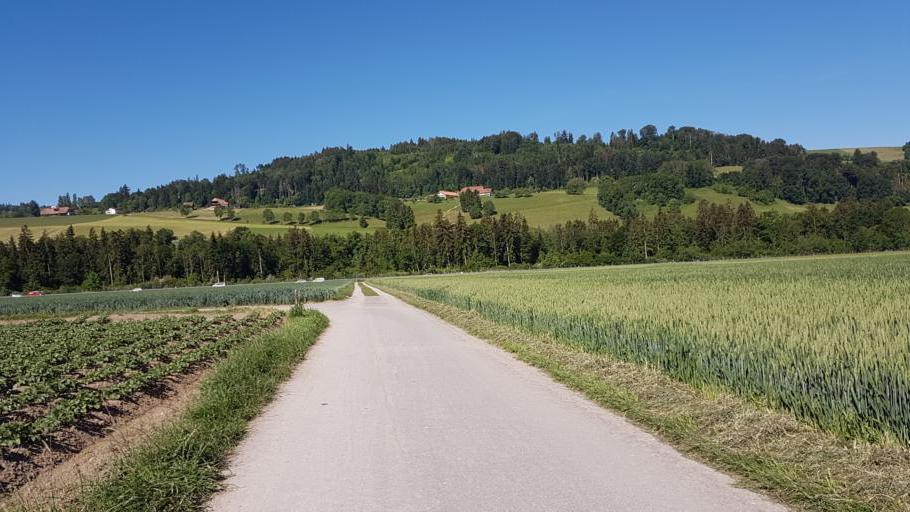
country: CH
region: Bern
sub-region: Bern-Mittelland District
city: Niederwichtrach
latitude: 46.8536
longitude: 7.5614
